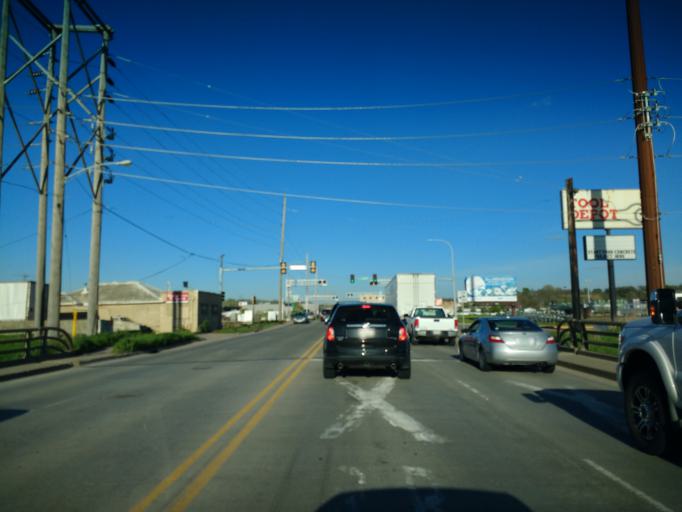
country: US
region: Iowa
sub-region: Woodbury County
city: Sioux City
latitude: 42.4887
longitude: -96.3913
